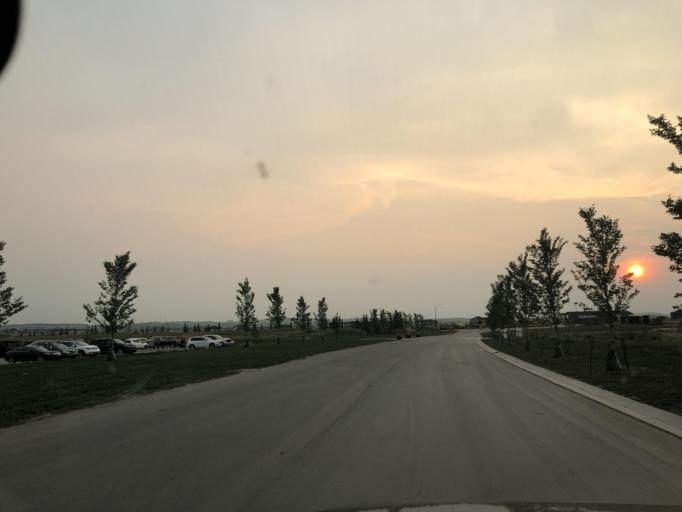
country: CA
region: Alberta
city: Cochrane
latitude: 51.1198
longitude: -114.3837
